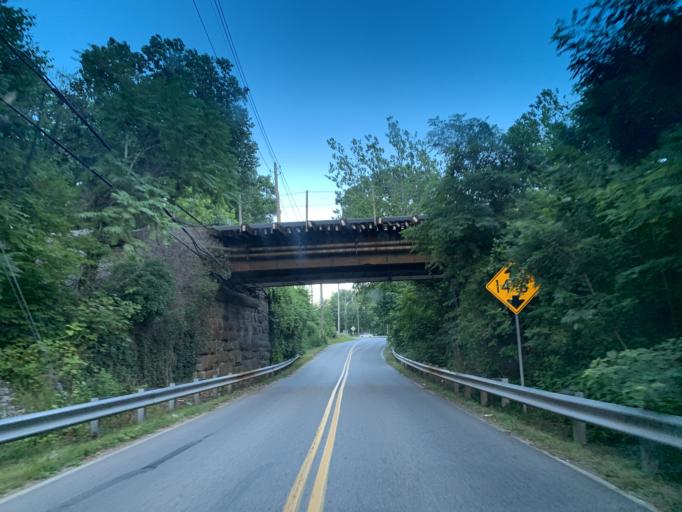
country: US
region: Maryland
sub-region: Harford County
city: Aberdeen
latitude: 39.5252
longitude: -76.1410
